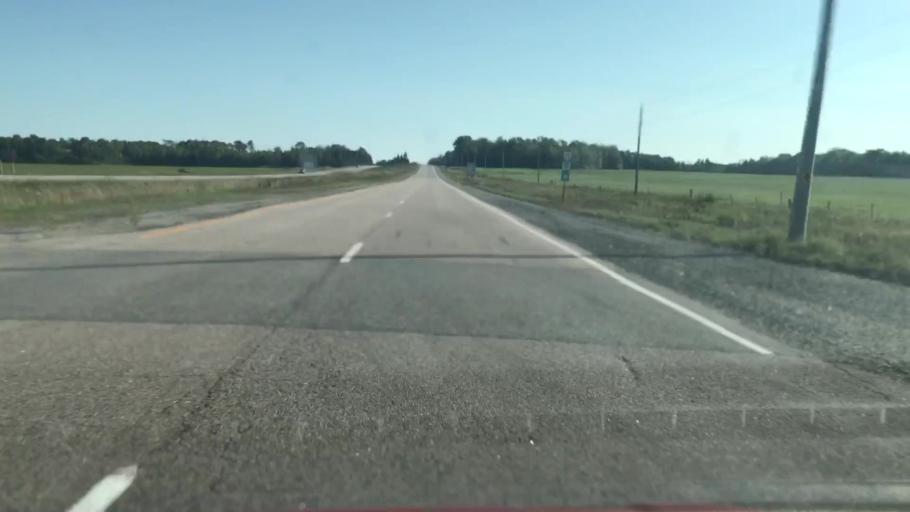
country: CA
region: Ontario
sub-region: Algoma
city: Sault Ste. Marie
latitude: 46.3544
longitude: -84.0679
